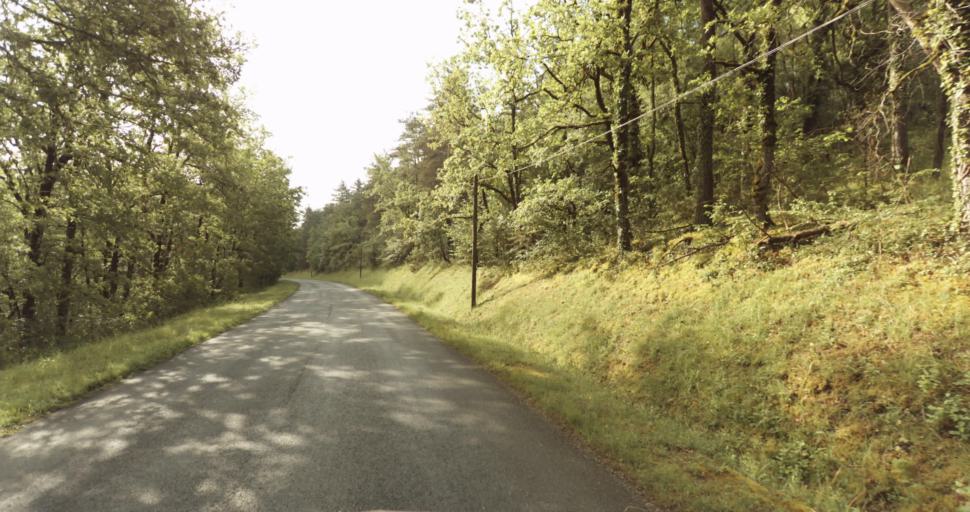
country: FR
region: Aquitaine
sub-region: Departement de la Dordogne
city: Lalinde
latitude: 44.9145
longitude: 0.7990
